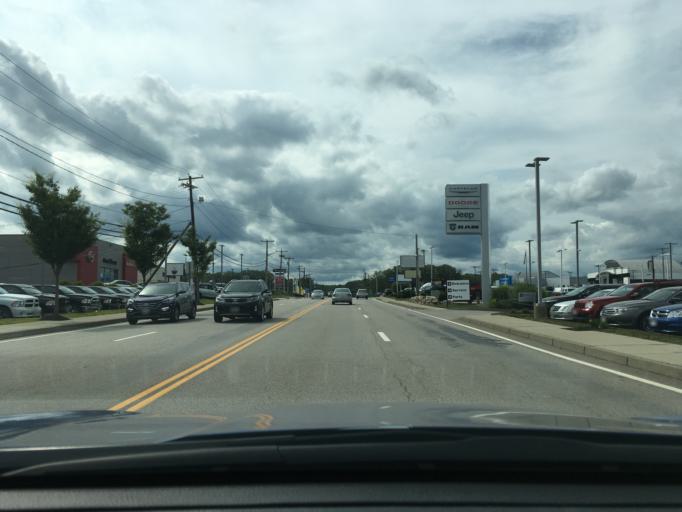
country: US
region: Rhode Island
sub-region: Providence County
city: Johnston
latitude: 41.8266
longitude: -71.5098
